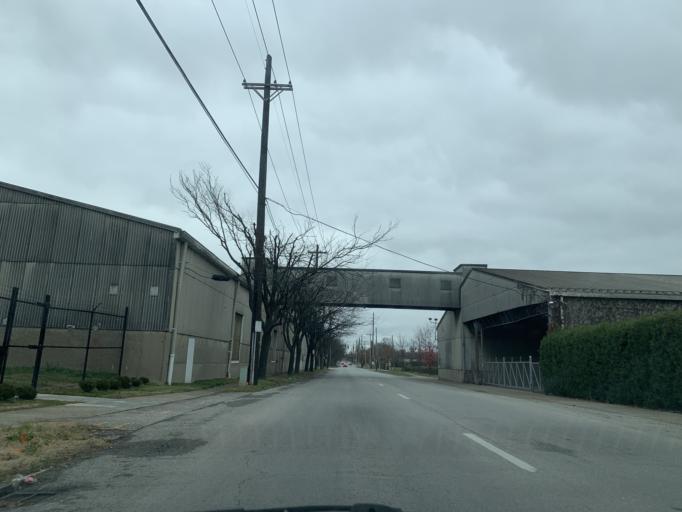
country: US
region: Kentucky
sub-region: Jefferson County
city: Louisville
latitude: 38.2457
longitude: -85.7872
